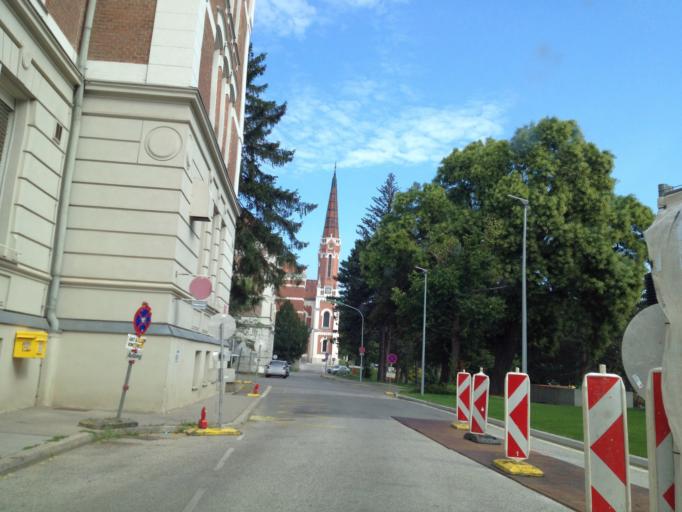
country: AT
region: Lower Austria
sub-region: Politischer Bezirk Modling
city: Perchtoldsdorf
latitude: 48.1714
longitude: 16.2757
